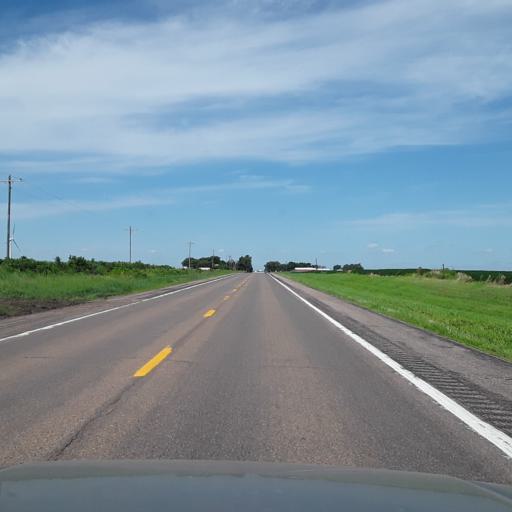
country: US
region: Nebraska
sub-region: Seward County
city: Seward
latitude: 40.9017
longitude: -97.1628
